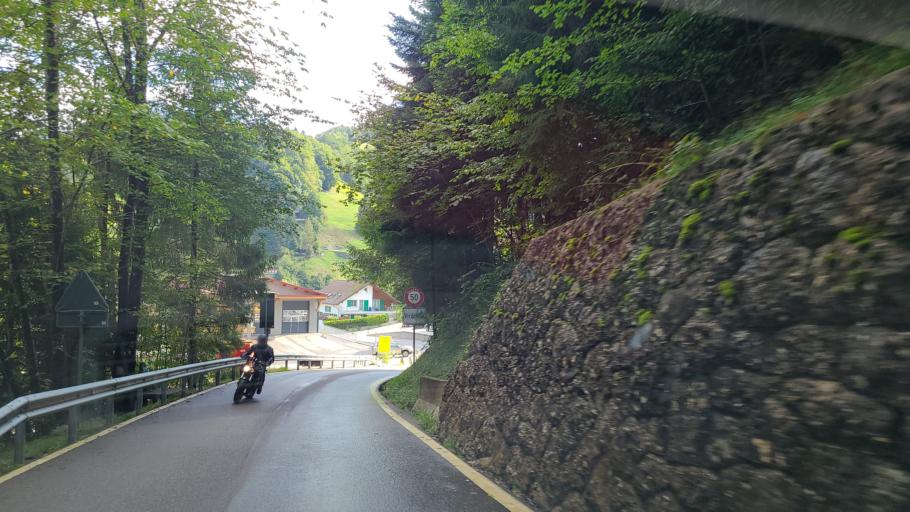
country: CH
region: Schwyz
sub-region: Bezirk March
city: Vorderthal
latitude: 47.1295
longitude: 8.8845
